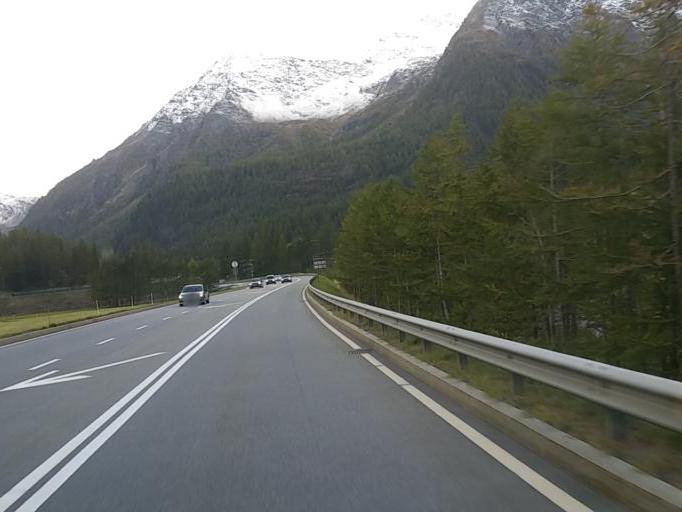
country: CH
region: Valais
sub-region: Brig District
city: Brig
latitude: 46.2090
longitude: 8.0415
